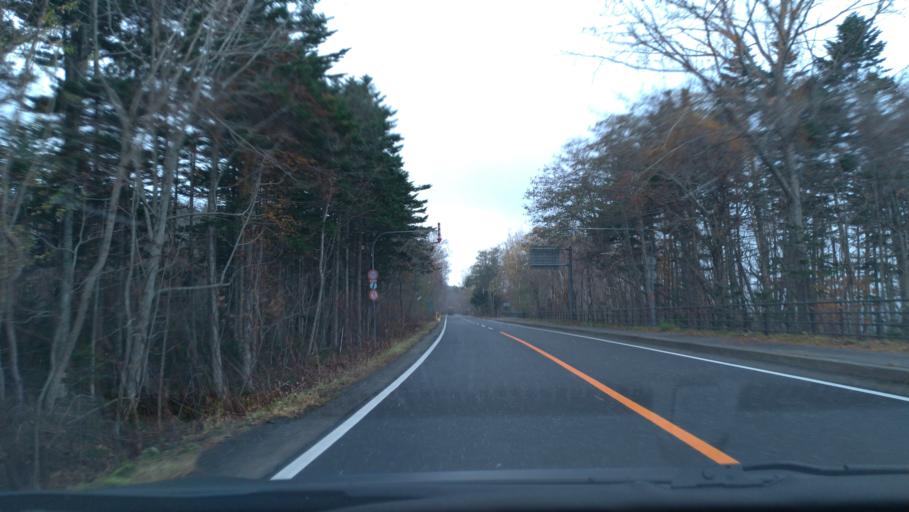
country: JP
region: Hokkaido
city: Shiraoi
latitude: 42.7421
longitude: 141.4016
